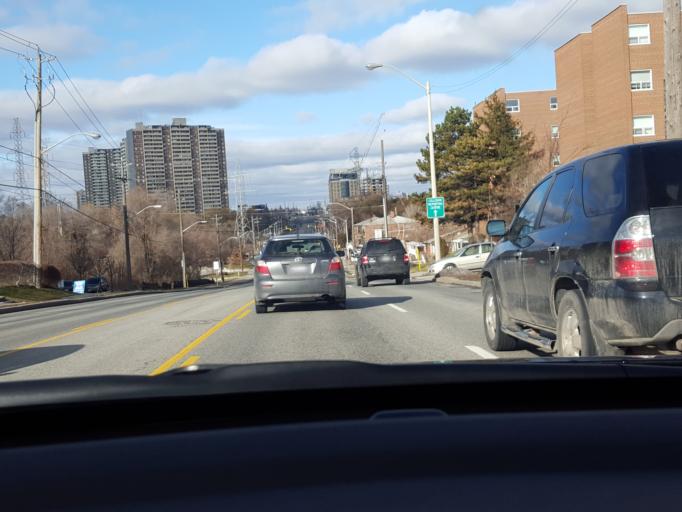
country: CA
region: Ontario
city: Concord
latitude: 43.7437
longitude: -79.5405
